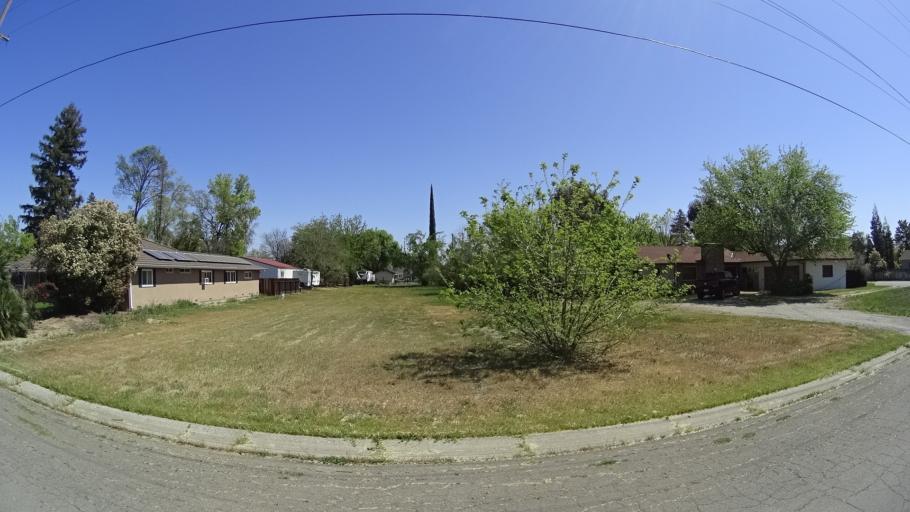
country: US
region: California
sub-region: Glenn County
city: Willows
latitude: 39.5259
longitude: -122.2074
